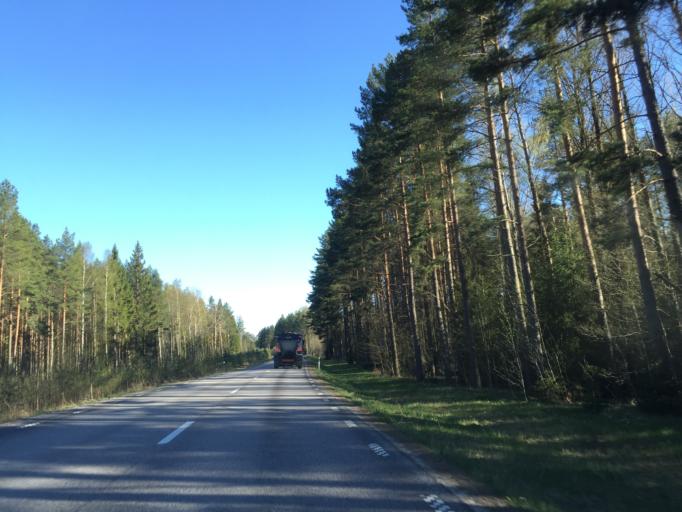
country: SE
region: OErebro
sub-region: Hallsbergs Kommun
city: Skollersta
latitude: 59.2418
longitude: 15.4021
